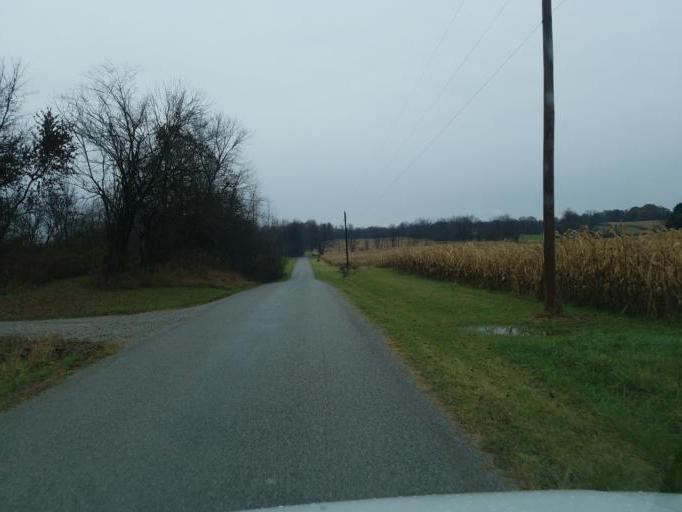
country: US
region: Ohio
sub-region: Knox County
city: Centerburg
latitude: 40.3607
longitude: -82.7100
